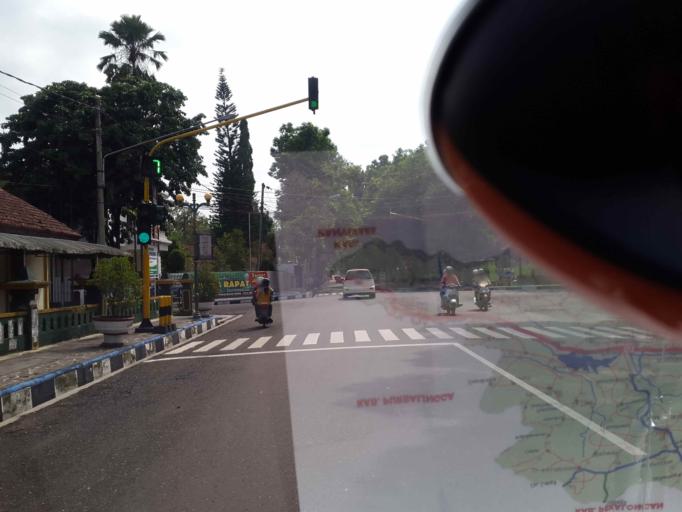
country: ID
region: Central Java
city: Wonosobo
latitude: -7.3952
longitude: 109.6953
